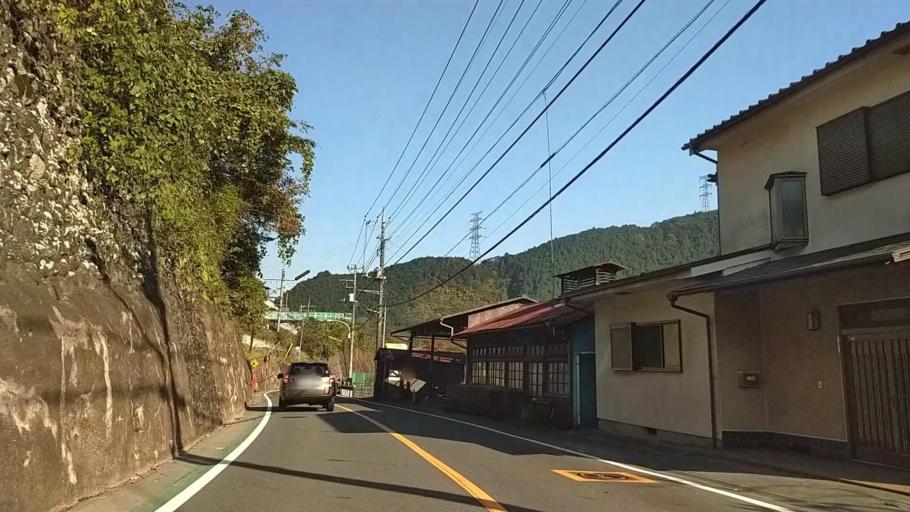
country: JP
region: Tokyo
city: Ome
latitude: 35.8010
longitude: 139.1789
